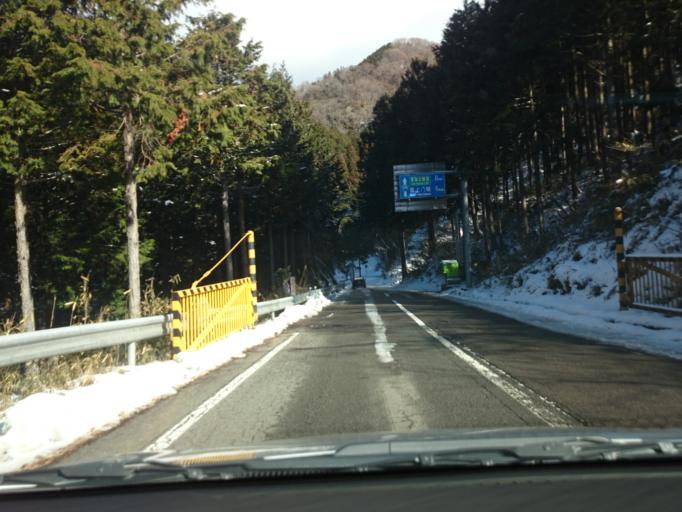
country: JP
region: Gifu
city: Gujo
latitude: 35.7410
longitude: 136.9844
